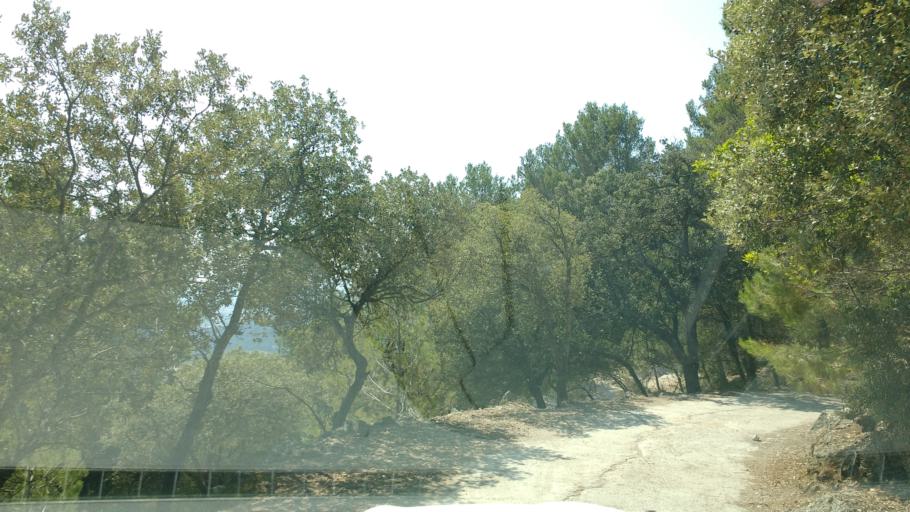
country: ES
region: Balearic Islands
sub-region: Illes Balears
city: Alaro
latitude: 39.7302
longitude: 2.7868
